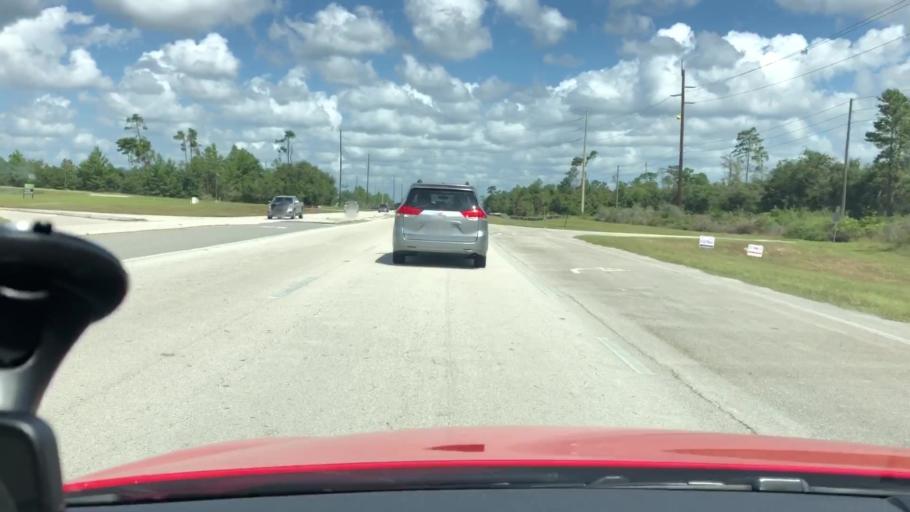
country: US
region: Florida
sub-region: Volusia County
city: Deltona
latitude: 28.9179
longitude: -81.2818
